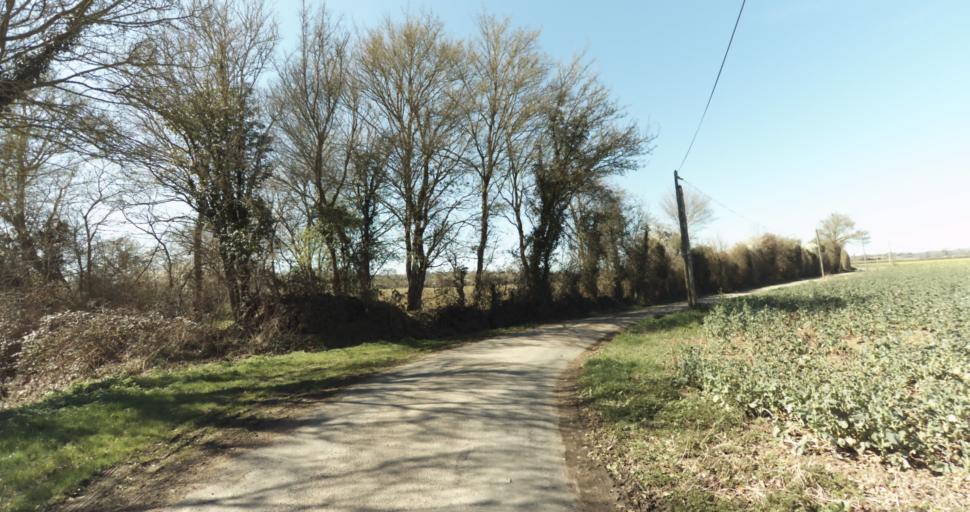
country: FR
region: Lower Normandy
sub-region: Departement du Calvados
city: Saint-Pierre-sur-Dives
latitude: 49.0318
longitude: 0.0112
